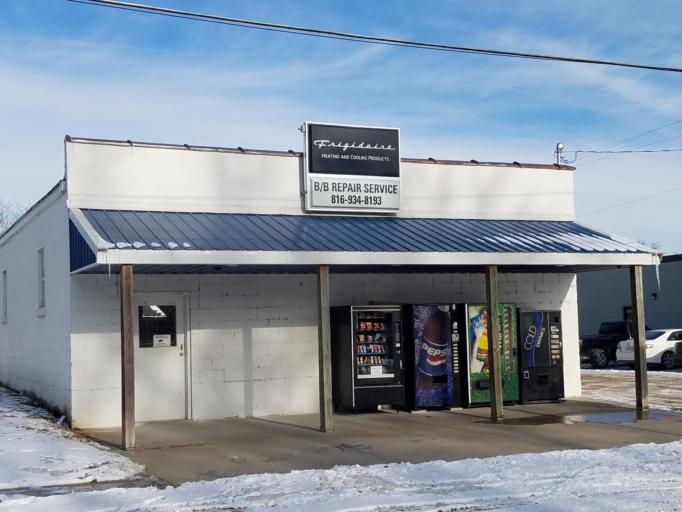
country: US
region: Missouri
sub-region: Lafayette County
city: Lexington
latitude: 39.1340
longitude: -93.9845
